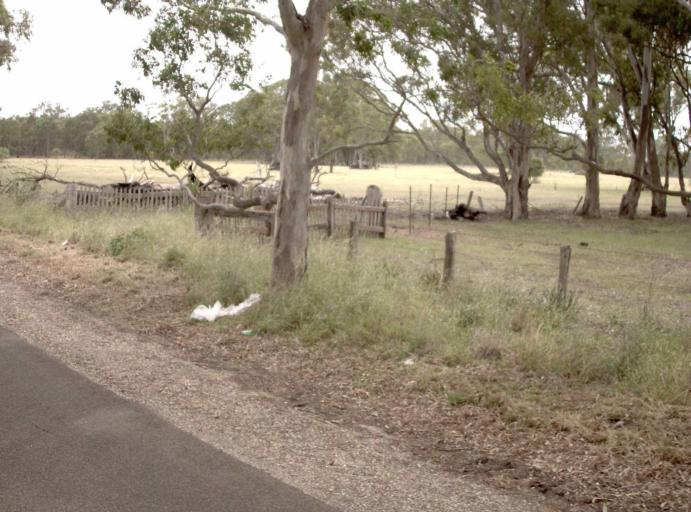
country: AU
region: Victoria
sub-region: Wellington
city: Sale
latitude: -37.8670
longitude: 147.0680
